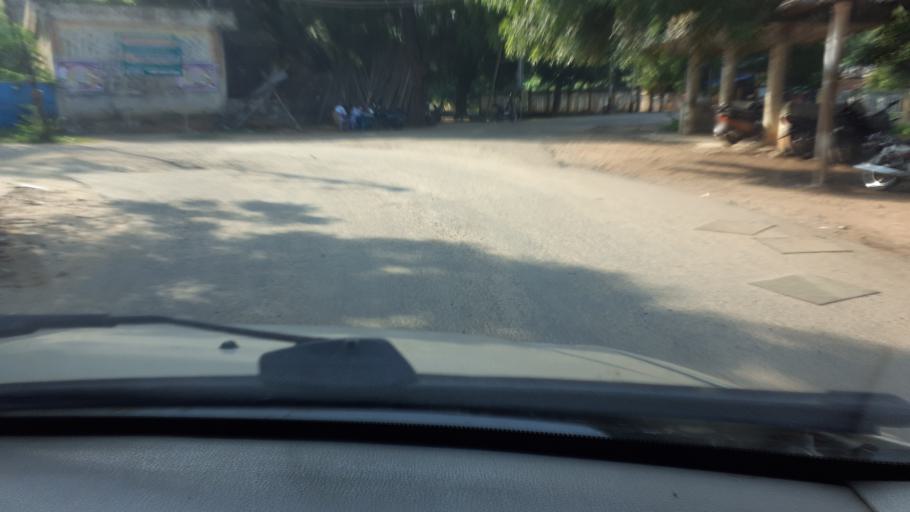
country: IN
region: Tamil Nadu
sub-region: Thoothukkudi
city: Eral
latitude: 8.5787
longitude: 78.0222
